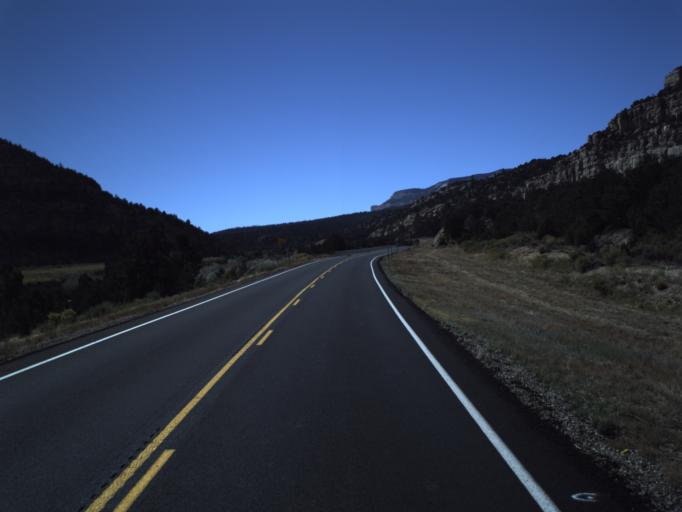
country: US
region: Utah
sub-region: Garfield County
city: Panguitch
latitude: 37.7299
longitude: -111.7613
